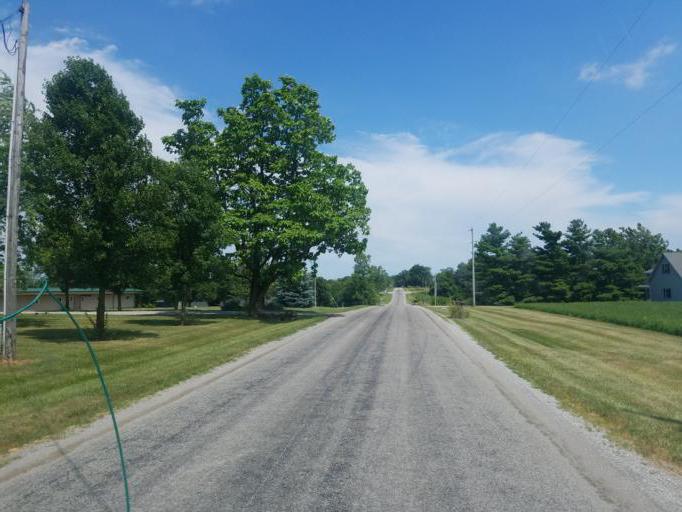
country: US
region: Indiana
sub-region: Allen County
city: Woodburn
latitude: 41.1683
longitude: -84.8631
